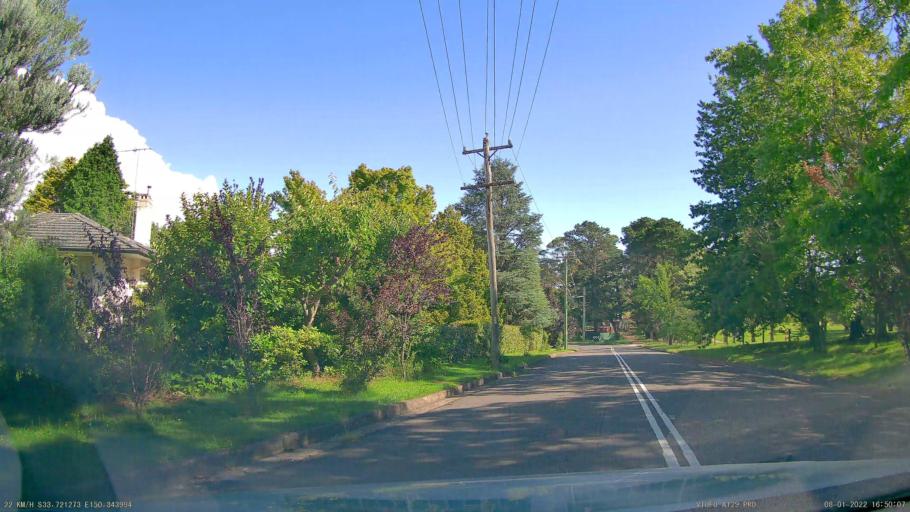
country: AU
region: New South Wales
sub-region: Blue Mountains Municipality
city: Leura
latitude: -33.7214
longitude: 150.3439
